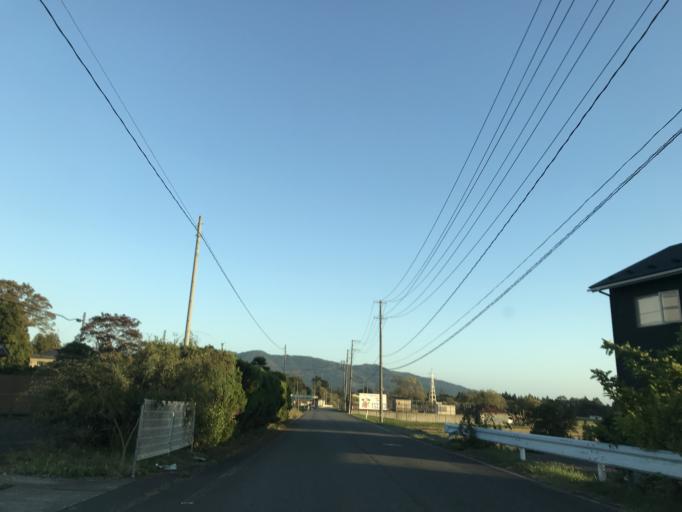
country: JP
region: Iwate
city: Mizusawa
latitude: 39.0546
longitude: 141.1153
